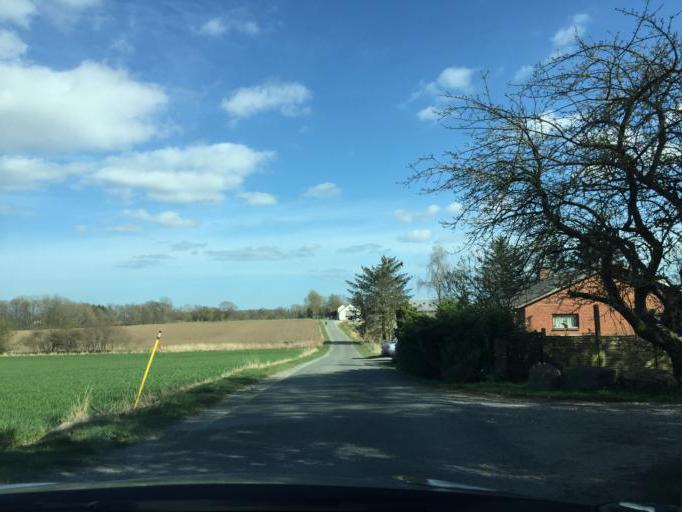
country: DK
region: South Denmark
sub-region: Kerteminde Kommune
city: Langeskov
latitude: 55.3061
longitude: 10.5573
